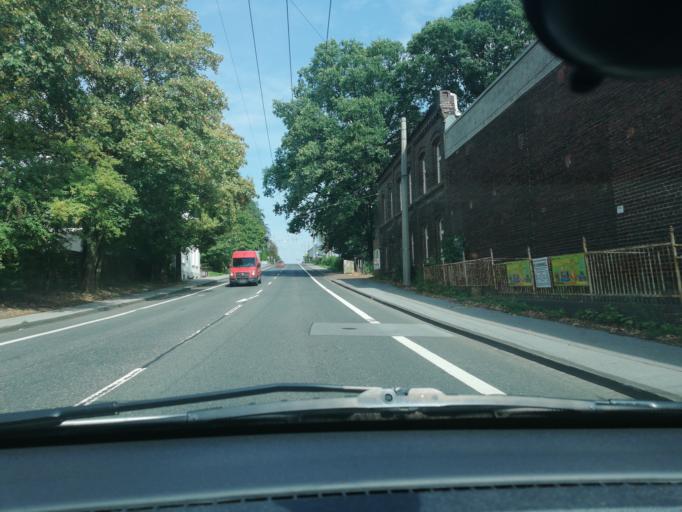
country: DE
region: North Rhine-Westphalia
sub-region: Regierungsbezirk Dusseldorf
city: Solingen
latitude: 51.2161
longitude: 7.0712
